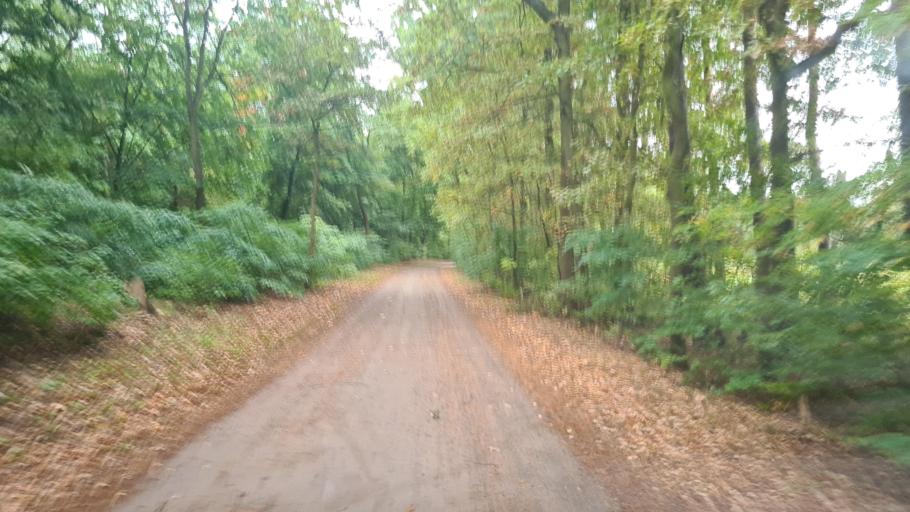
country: DE
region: Brandenburg
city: Storkow
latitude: 52.2282
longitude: 13.9337
